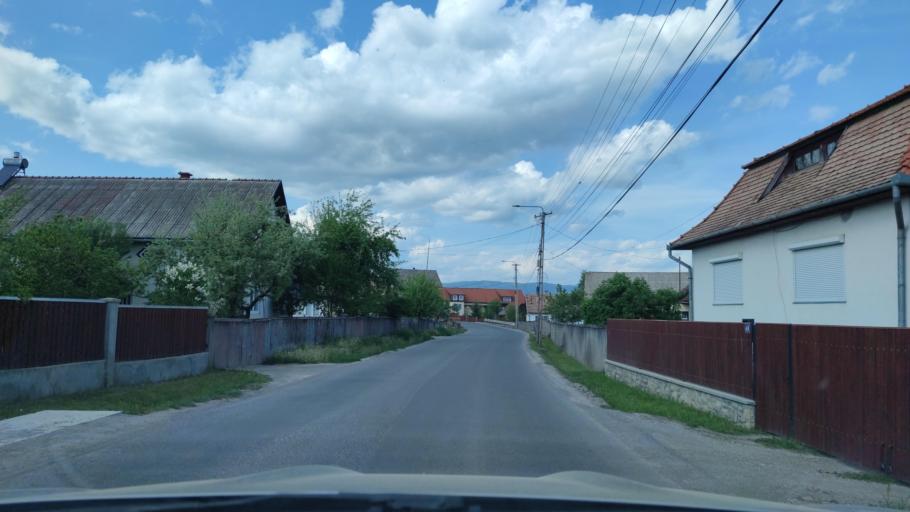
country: RO
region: Harghita
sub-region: Comuna Remetea
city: Remetea
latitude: 46.8045
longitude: 25.4599
